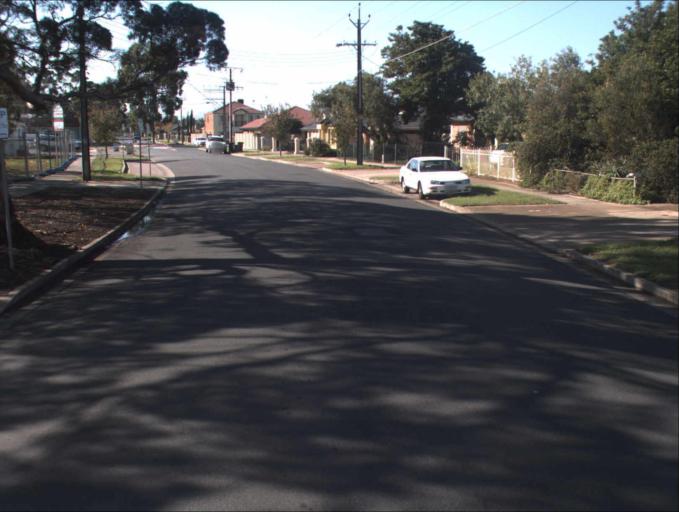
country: AU
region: South Australia
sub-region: Charles Sturt
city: Woodville North
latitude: -34.8593
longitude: 138.5553
